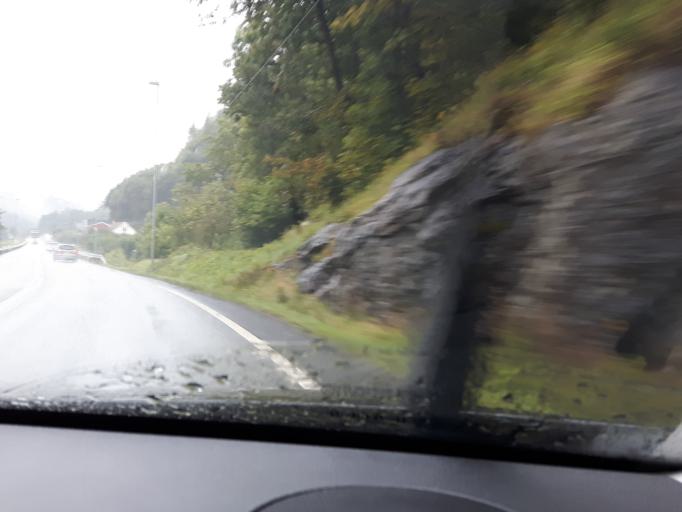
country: NO
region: Vest-Agder
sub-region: Mandal
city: Mandal
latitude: 58.0468
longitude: 7.4162
